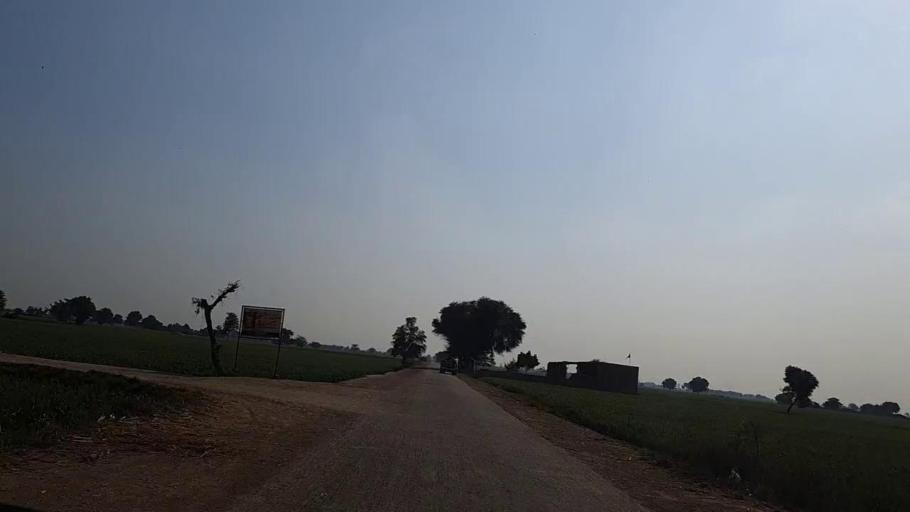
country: PK
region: Sindh
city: Sakrand
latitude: 26.0922
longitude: 68.2904
